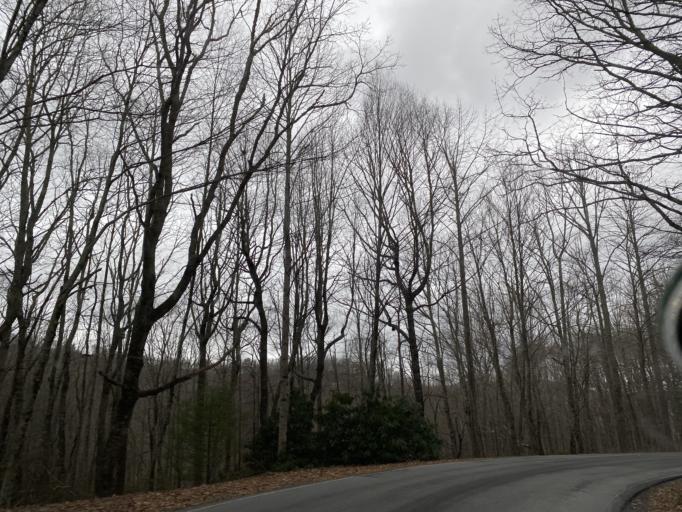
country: US
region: North Carolina
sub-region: Jackson County
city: Cullowhee
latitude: 35.2149
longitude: -83.1817
